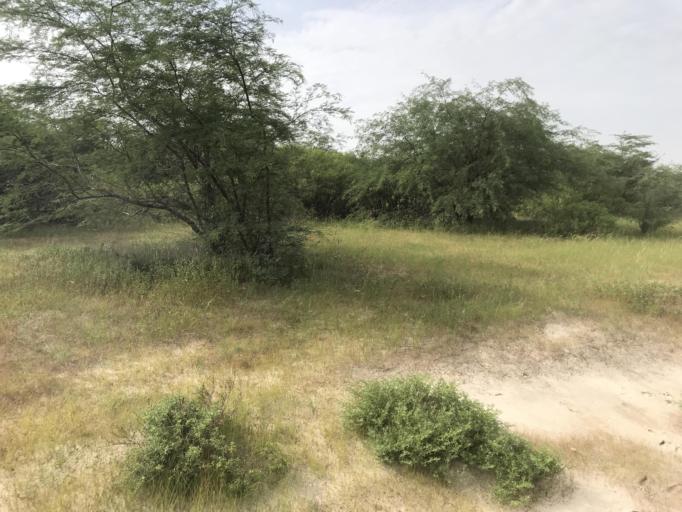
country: SN
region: Saint-Louis
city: Saint-Louis
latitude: 15.9262
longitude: -16.4659
